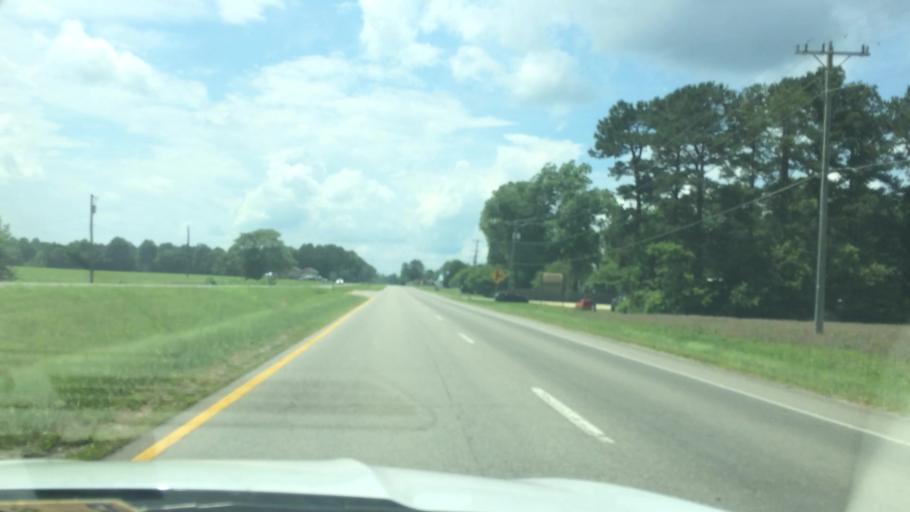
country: US
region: Virginia
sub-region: King William County
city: West Point
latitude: 37.5453
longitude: -76.7105
